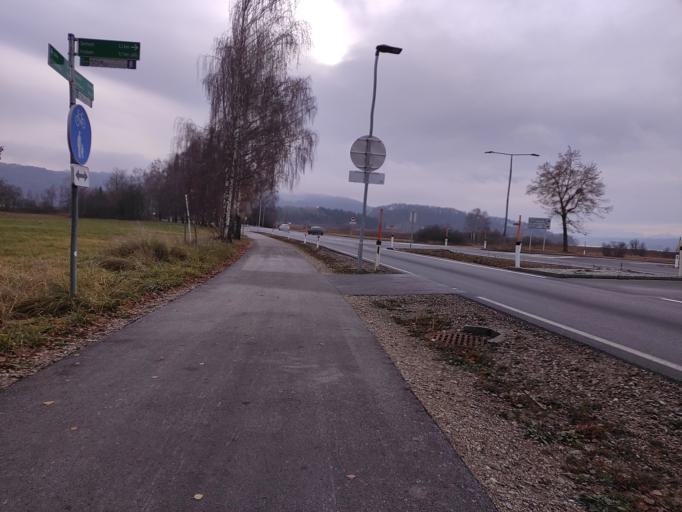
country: AT
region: Salzburg
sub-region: Politischer Bezirk Salzburg-Umgebung
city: Mattsee
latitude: 47.9836
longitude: 13.1037
